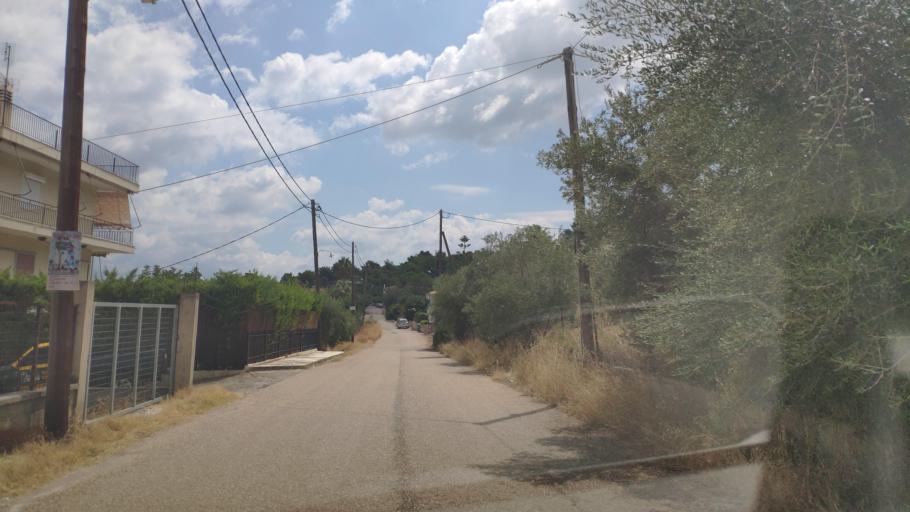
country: GR
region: Central Greece
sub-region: Nomos Fthiotidos
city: Malesina
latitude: 38.6476
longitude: 23.1896
